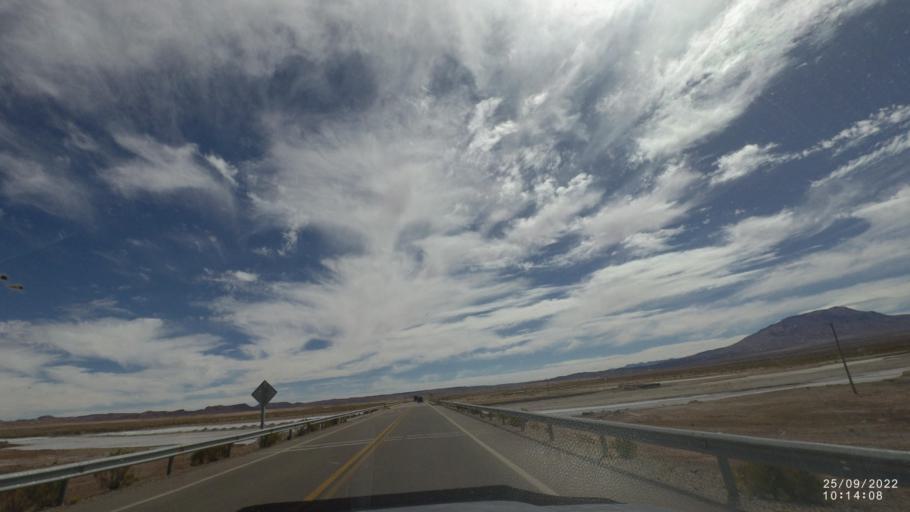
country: BO
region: Potosi
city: Colchani
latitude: -20.0651
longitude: -66.8823
